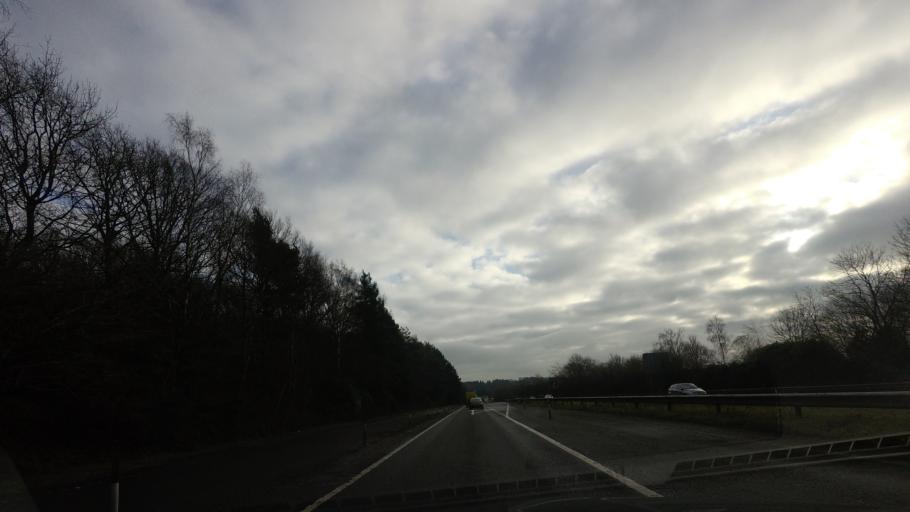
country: GB
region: England
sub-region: Kent
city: Hawkhurst
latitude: 51.0639
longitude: 0.4412
